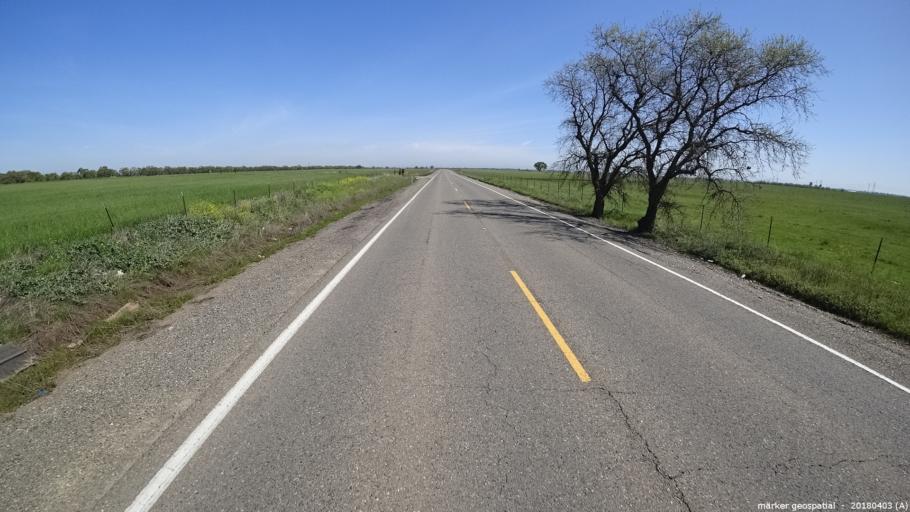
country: US
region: California
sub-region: Sacramento County
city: Elk Grove
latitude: 38.3532
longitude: -121.3225
